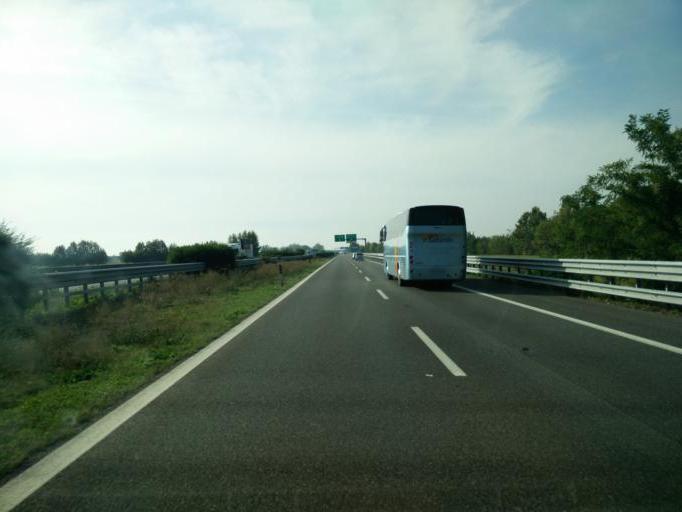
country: IT
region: Lombardy
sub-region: Provincia di Brescia
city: Alfianello
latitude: 45.2823
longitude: 10.1323
